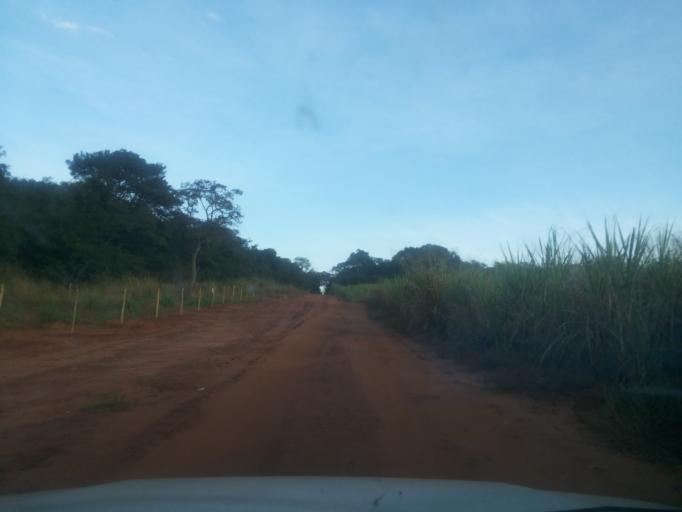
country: BR
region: Minas Gerais
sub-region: Santa Vitoria
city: Santa Vitoria
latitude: -19.0036
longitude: -50.3732
